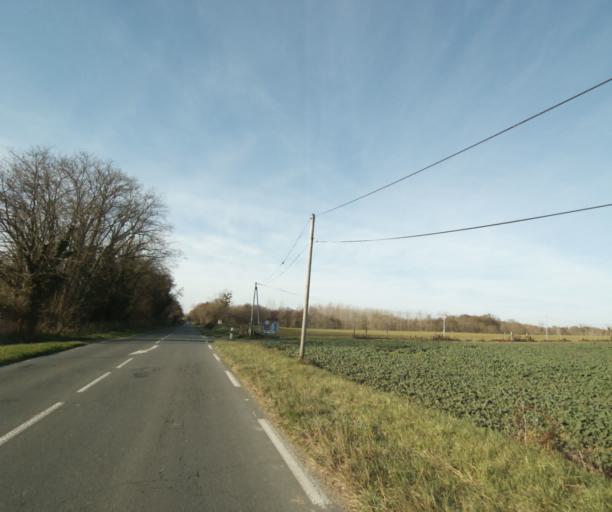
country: FR
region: Poitou-Charentes
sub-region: Departement de la Charente-Maritime
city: Chaniers
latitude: 45.7106
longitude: -0.5330
